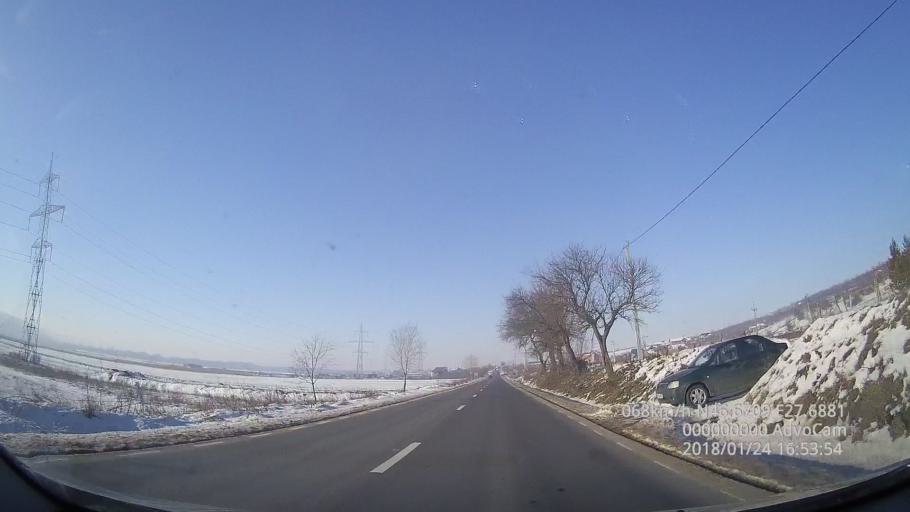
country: RO
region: Vaslui
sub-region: Municipiul Vaslui
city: Brodoc
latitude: 46.6712
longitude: 27.6878
